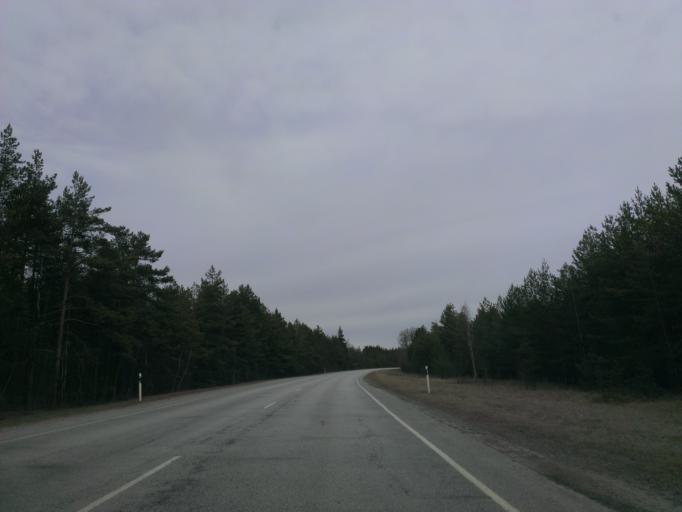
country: EE
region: Laeaene
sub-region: Lihula vald
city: Lihula
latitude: 58.6065
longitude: 23.5603
